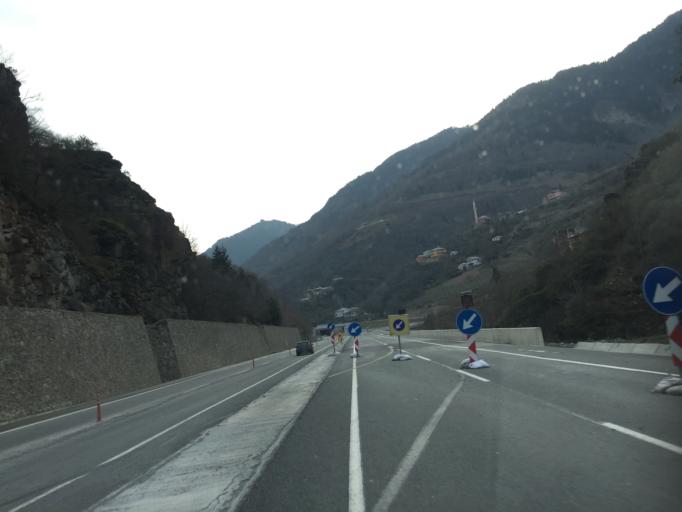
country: TR
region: Trabzon
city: Macka
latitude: 40.7825
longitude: 39.5730
